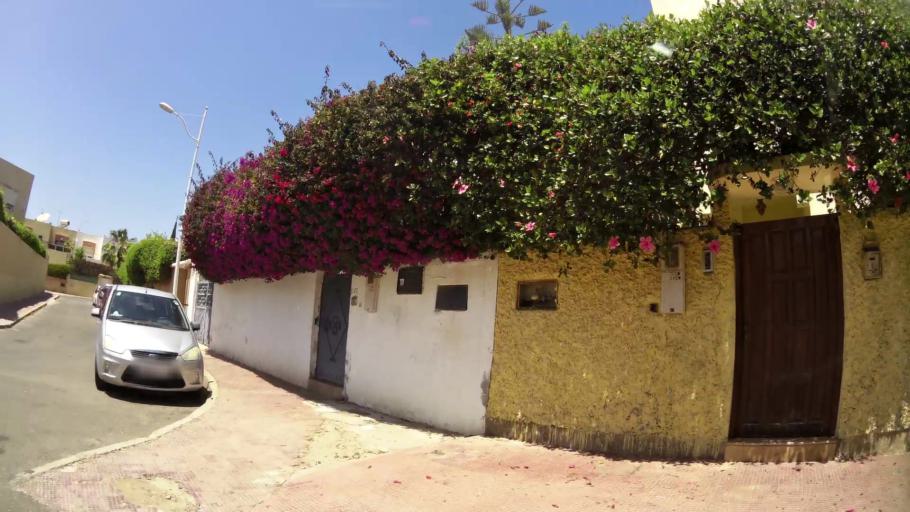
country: MA
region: Souss-Massa-Draa
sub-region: Agadir-Ida-ou-Tnan
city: Agadir
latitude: 30.4347
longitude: -9.5834
